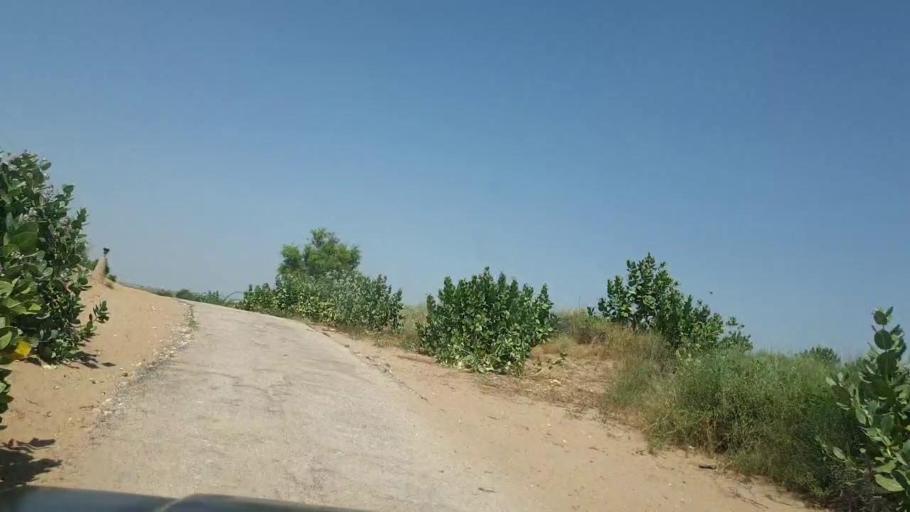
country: PK
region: Sindh
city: Chor
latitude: 25.3963
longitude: 70.3135
